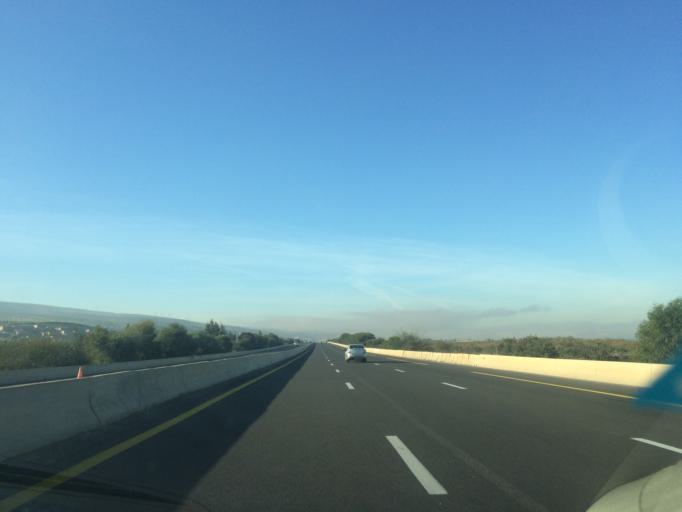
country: DZ
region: Relizane
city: Oued Rhiou
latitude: 36.0129
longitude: 1.0191
